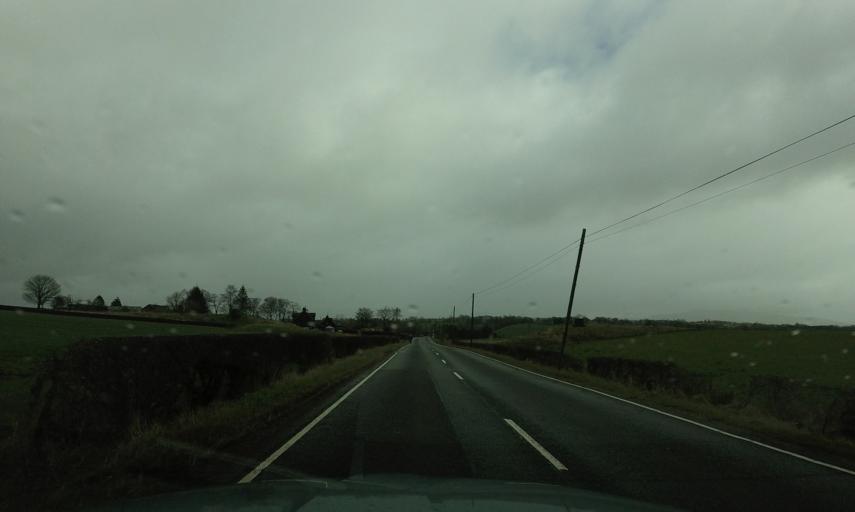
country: GB
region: Scotland
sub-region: Stirling
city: Killearn
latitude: 56.0790
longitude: -4.3782
